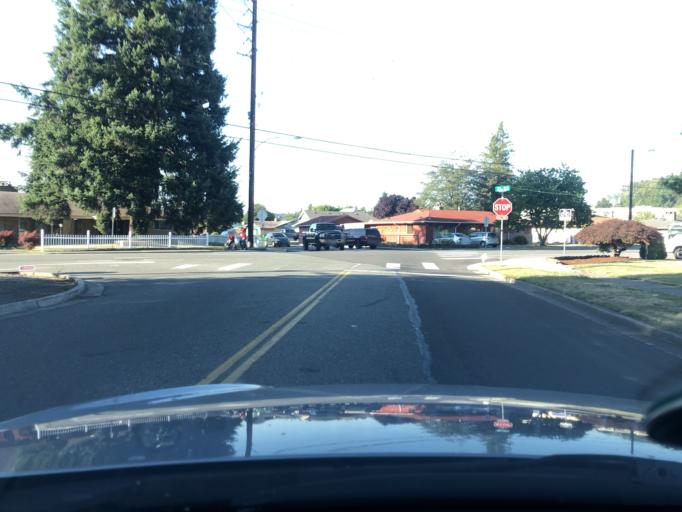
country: US
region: Washington
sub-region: King County
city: Auburn
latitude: 47.2898
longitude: -122.2132
